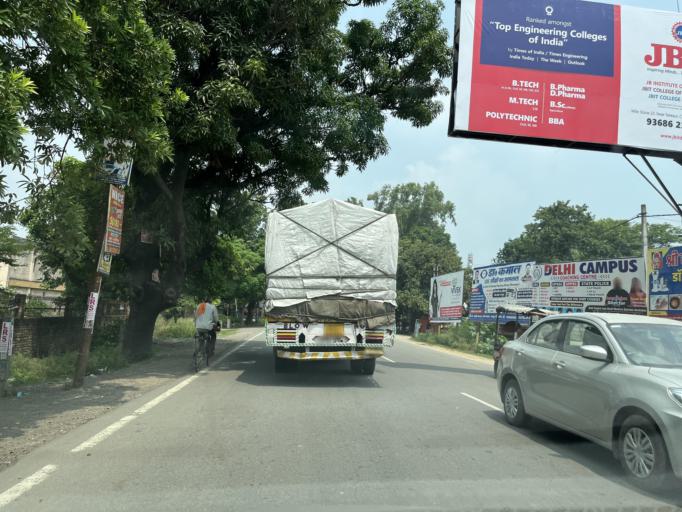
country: IN
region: Uttar Pradesh
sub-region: Bijnor
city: Najibabad
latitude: 29.5974
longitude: 78.3395
